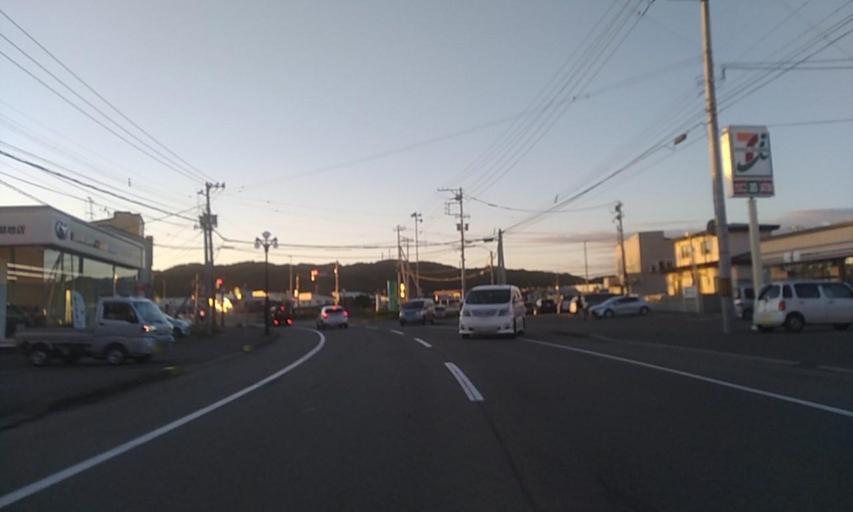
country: JP
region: Hokkaido
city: Shizunai-furukawacho
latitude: 42.1731
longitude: 142.7662
